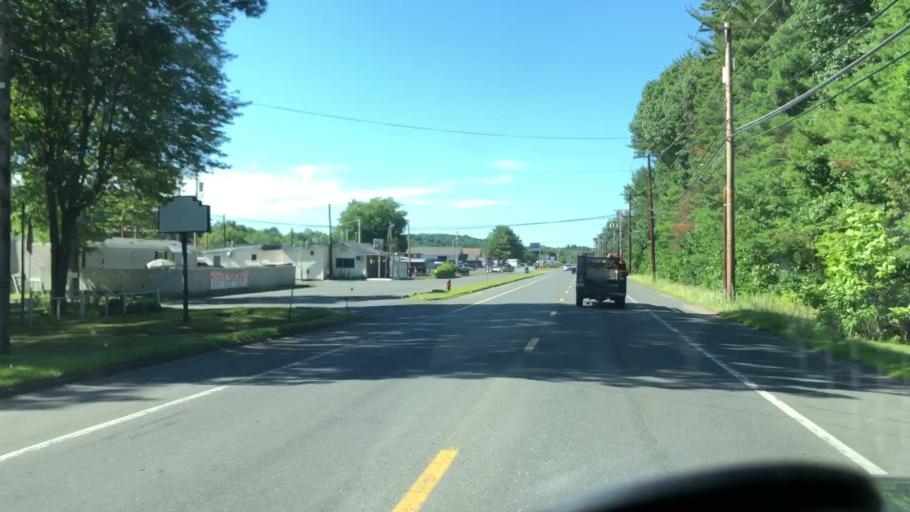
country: US
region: Massachusetts
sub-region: Hampden County
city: Westfield
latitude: 42.1685
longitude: -72.7267
